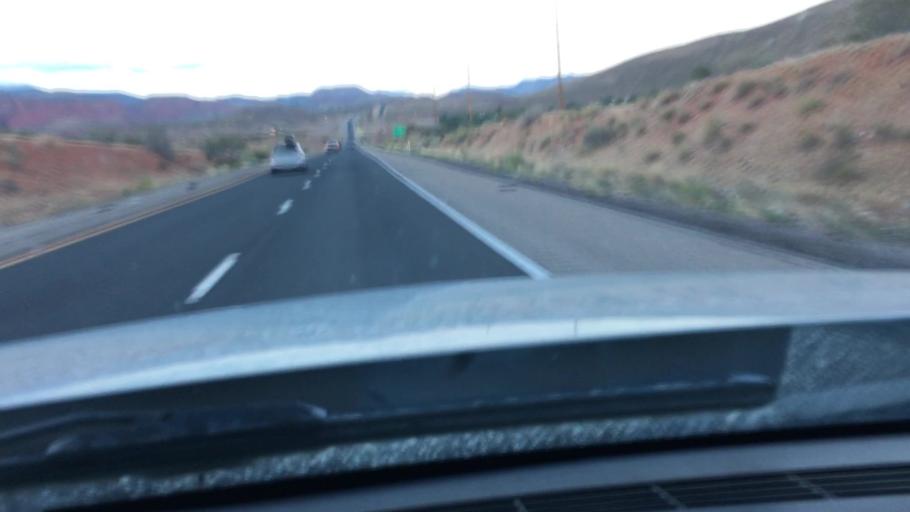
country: US
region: Utah
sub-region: Washington County
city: Hurricane
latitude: 37.1998
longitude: -113.3993
